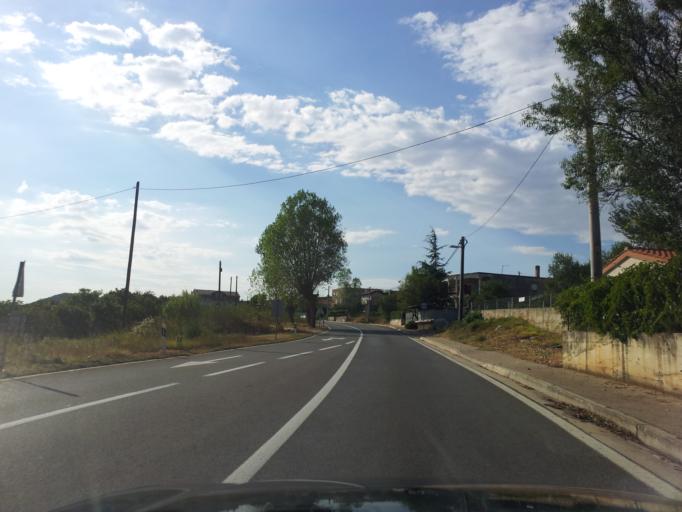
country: HR
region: Zadarska
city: Posedarje
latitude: 44.2160
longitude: 15.4673
